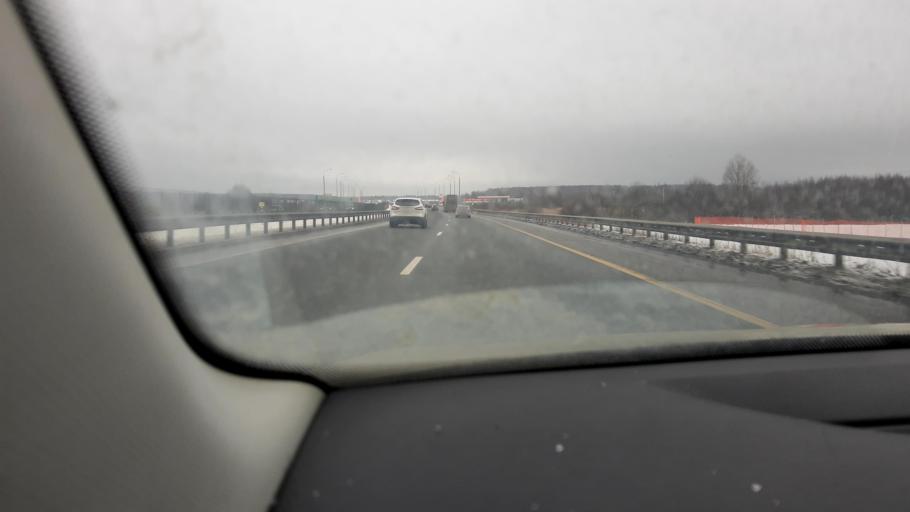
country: RU
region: Moskovskaya
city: Mikhnevo
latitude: 55.0963
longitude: 37.9286
